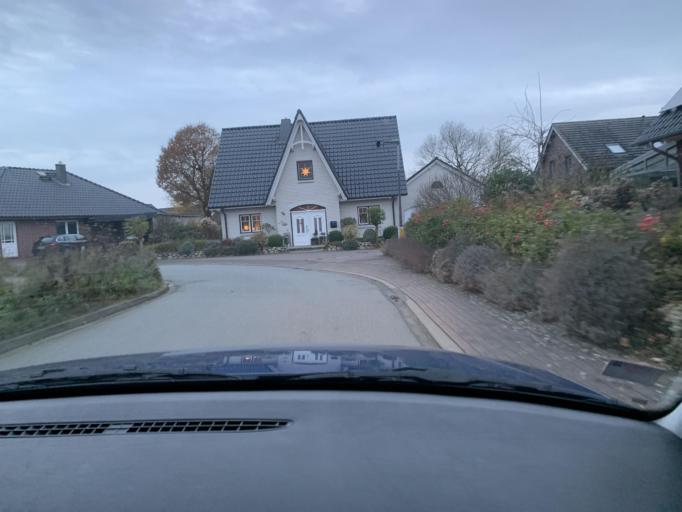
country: DE
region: Schleswig-Holstein
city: Lohe-Rickelshof
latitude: 54.2048
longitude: 9.0731
